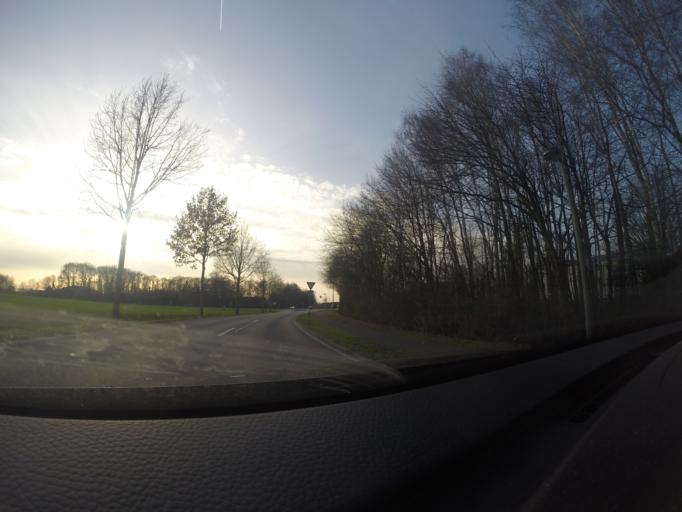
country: NL
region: Overijssel
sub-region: Gemeente Enschede
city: Enschede
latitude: 52.1264
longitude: 6.9082
